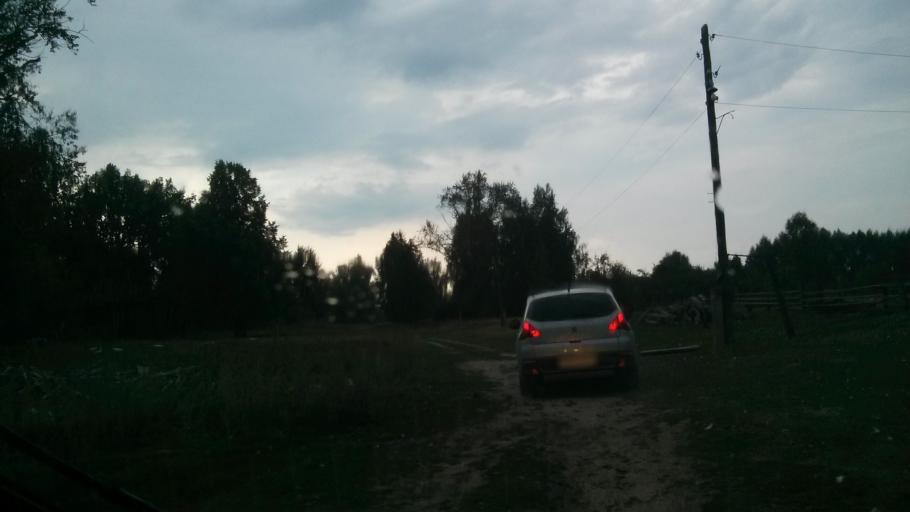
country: RU
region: Nizjnij Novgorod
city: Shimorskoye
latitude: 55.3109
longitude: 41.8654
